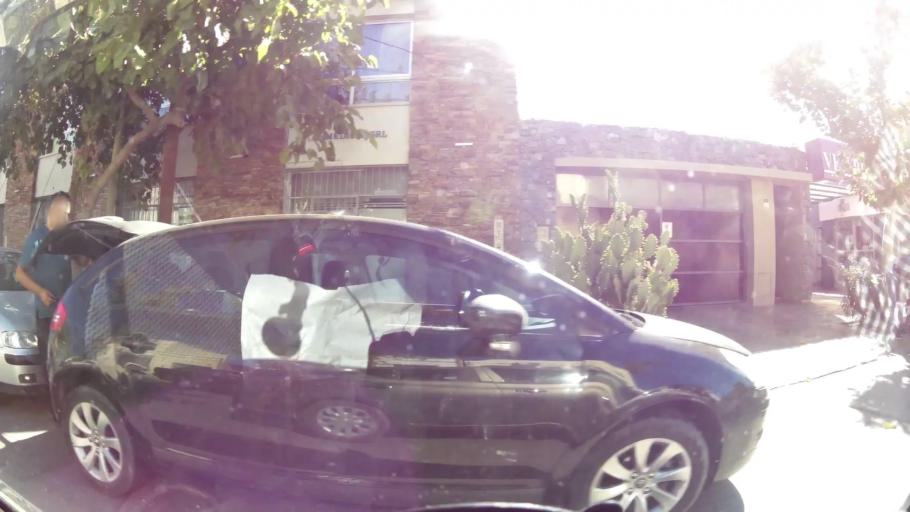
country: AR
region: San Juan
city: San Juan
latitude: -31.5431
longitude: -68.5343
